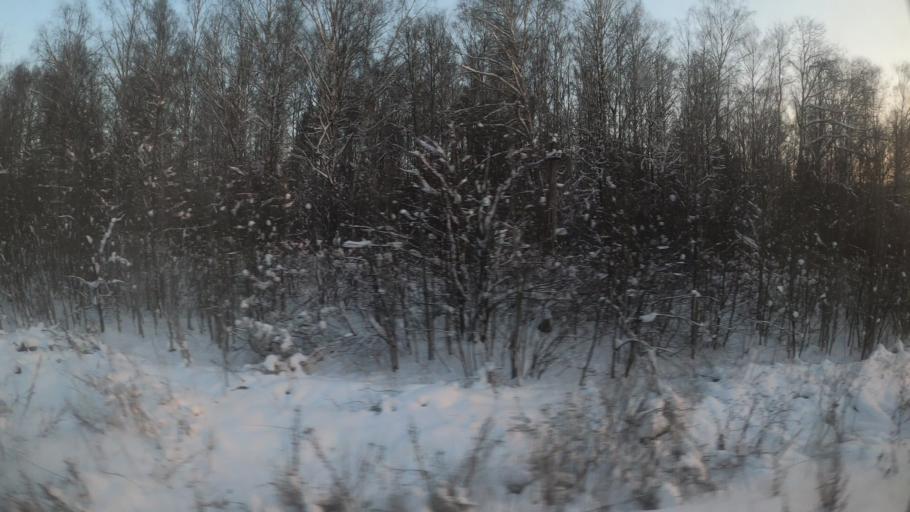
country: RU
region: Moskovskaya
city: Dedenevo
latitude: 56.2317
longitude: 37.5167
